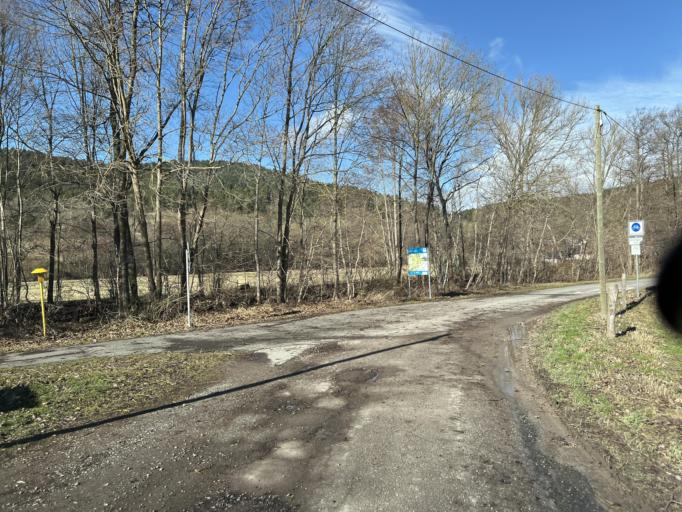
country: DE
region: Thuringia
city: Plaue
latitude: 50.7924
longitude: 10.9150
